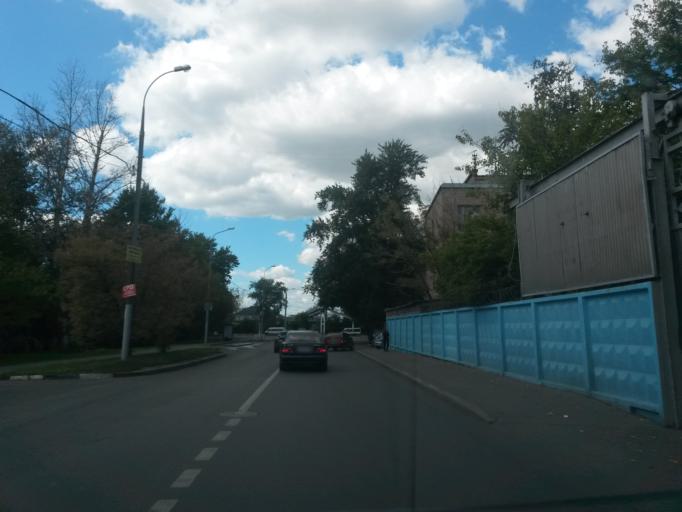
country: RU
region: Moscow
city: Mar'ino
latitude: 55.6594
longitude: 37.7219
